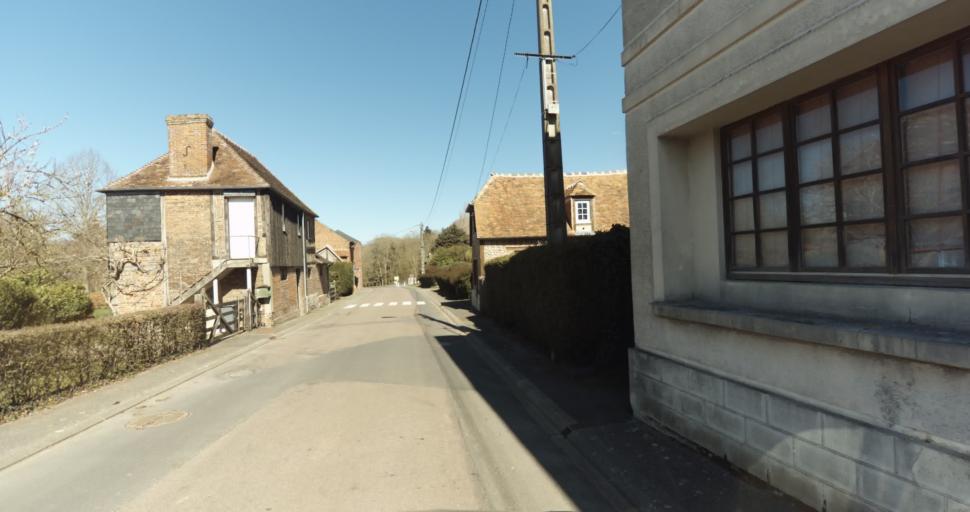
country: FR
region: Lower Normandy
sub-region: Departement du Calvados
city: Livarot
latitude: 48.9683
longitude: 0.0744
